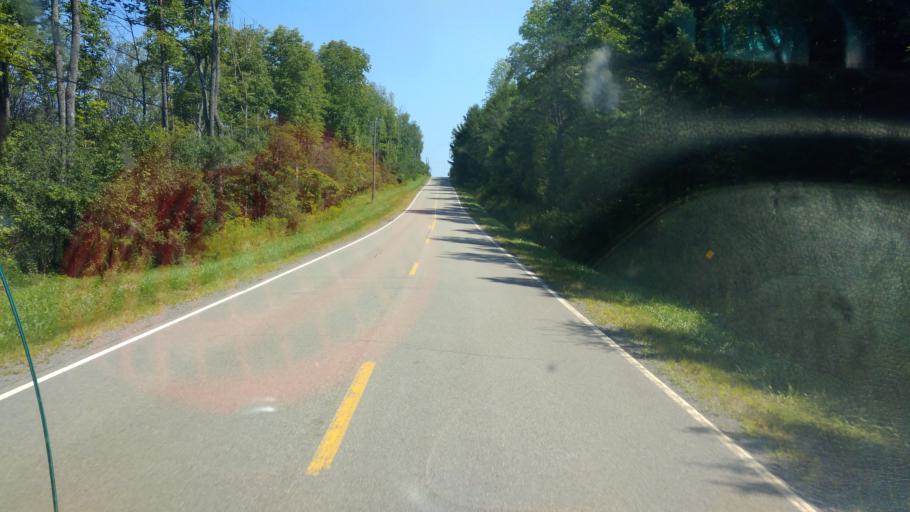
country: US
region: New York
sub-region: Allegany County
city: Alfred
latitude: 42.2960
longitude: -77.9023
